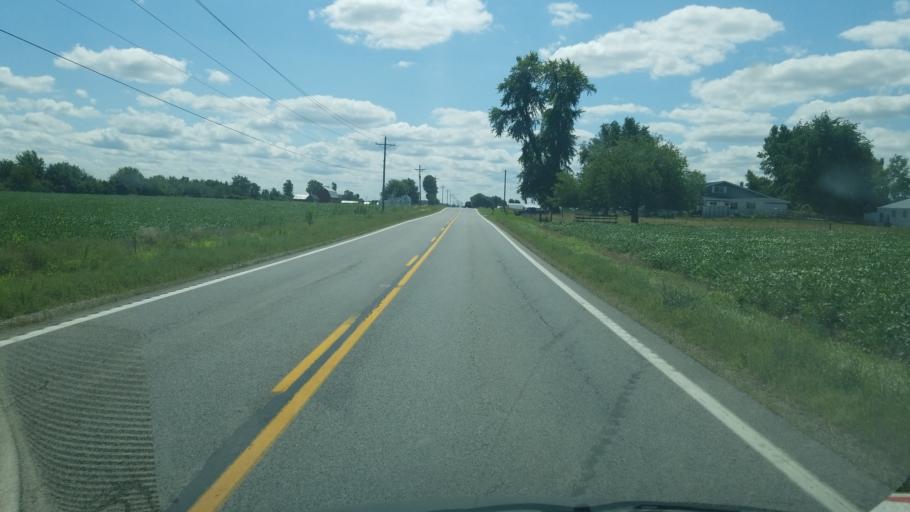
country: US
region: Ohio
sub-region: Fulton County
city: Delta
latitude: 41.6376
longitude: -84.0349
